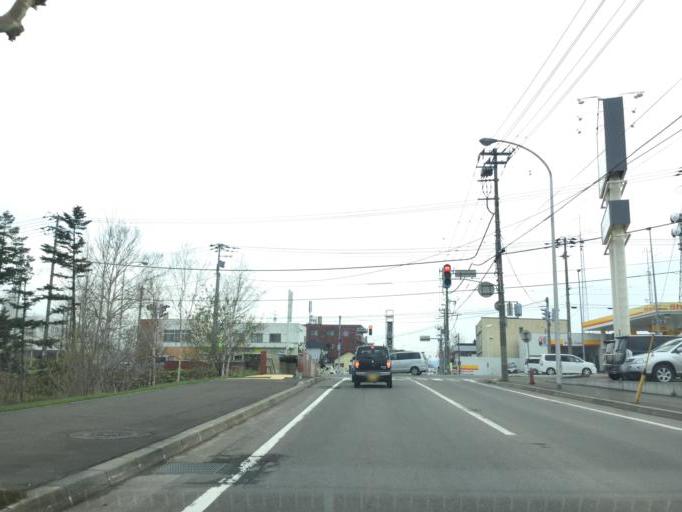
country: JP
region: Hokkaido
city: Iwamizawa
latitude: 43.2102
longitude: 141.7841
